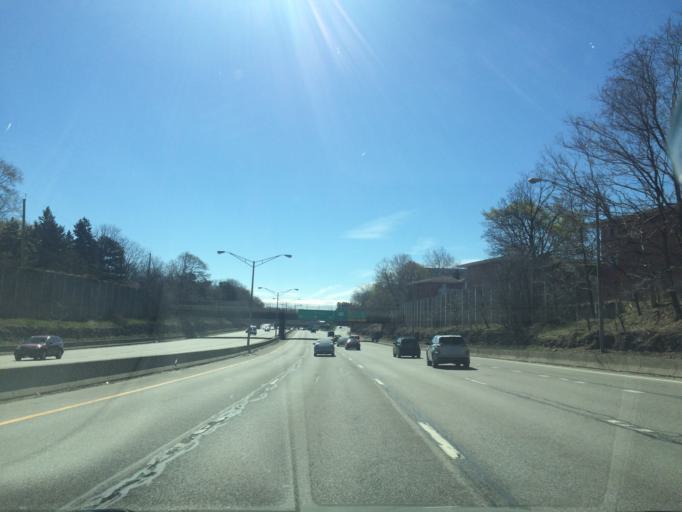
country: US
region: New York
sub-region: Monroe County
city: Brighton
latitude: 43.1405
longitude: -77.5414
